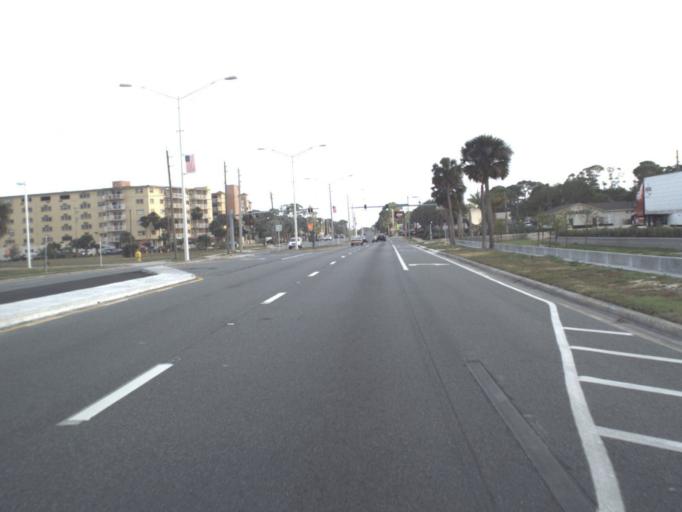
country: US
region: Florida
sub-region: Brevard County
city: Titusville
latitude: 28.5857
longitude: -80.8017
